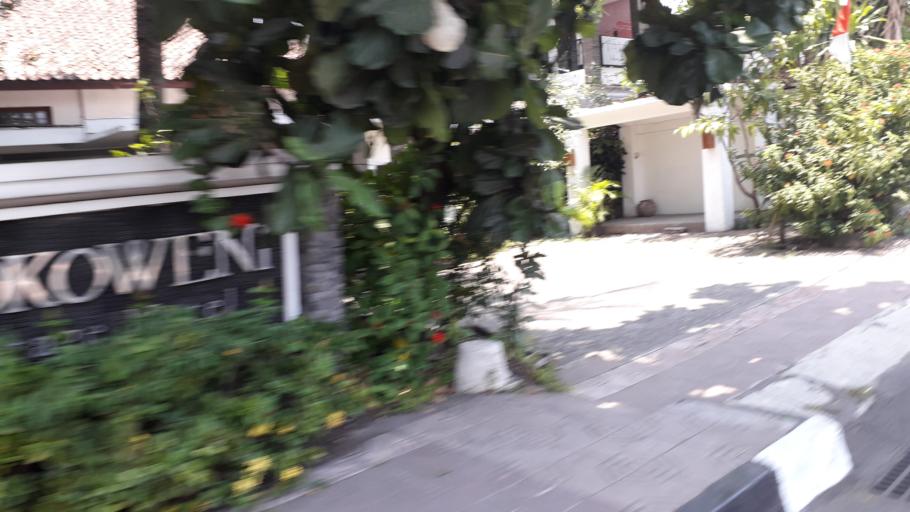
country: ID
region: Daerah Istimewa Yogyakarta
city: Yogyakarta
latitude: -7.7743
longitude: 110.3681
